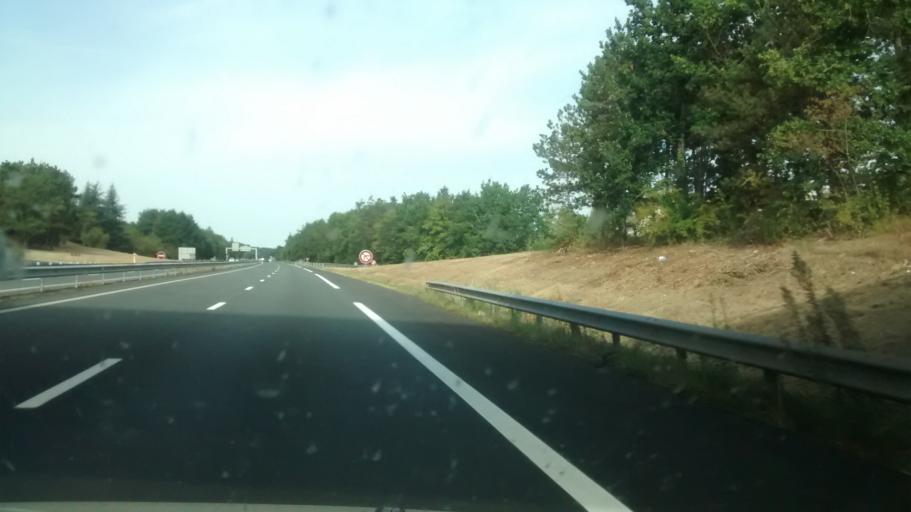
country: FR
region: Aquitaine
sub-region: Departement du Lot-et-Garonne
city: Boe
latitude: 44.1623
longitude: 0.6042
